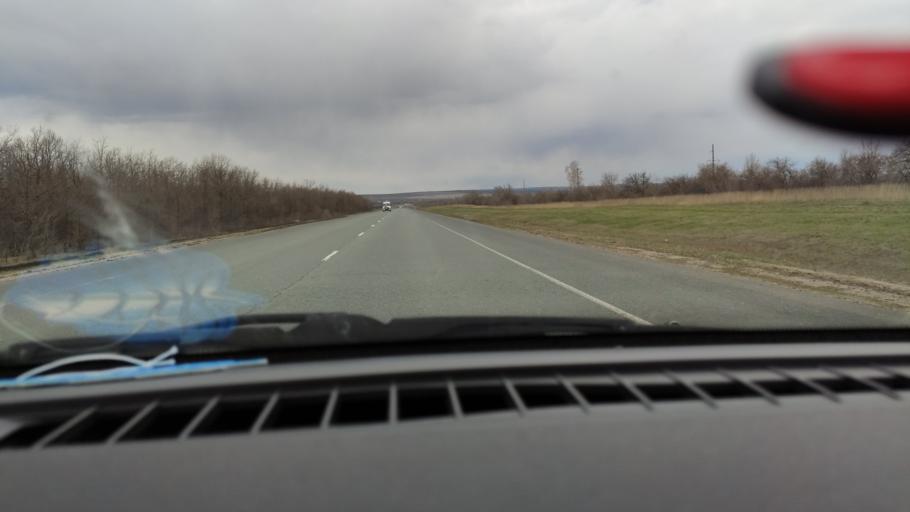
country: RU
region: Saratov
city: Yelshanka
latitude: 51.8273
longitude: 46.2707
